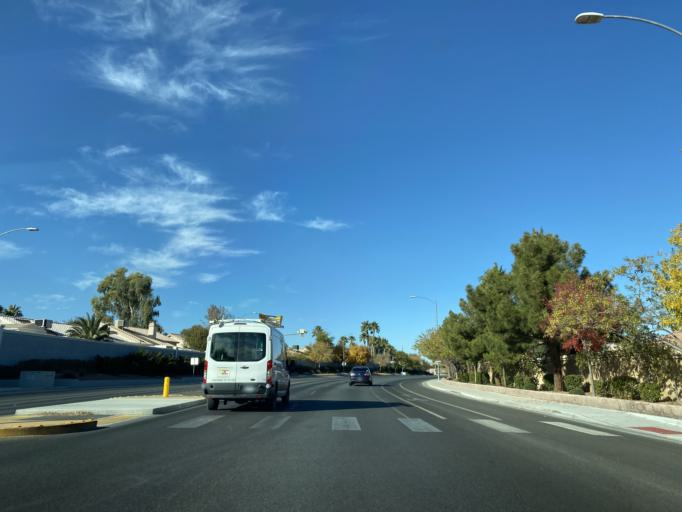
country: US
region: Nevada
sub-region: Clark County
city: Las Vegas
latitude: 36.2957
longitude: -115.2598
